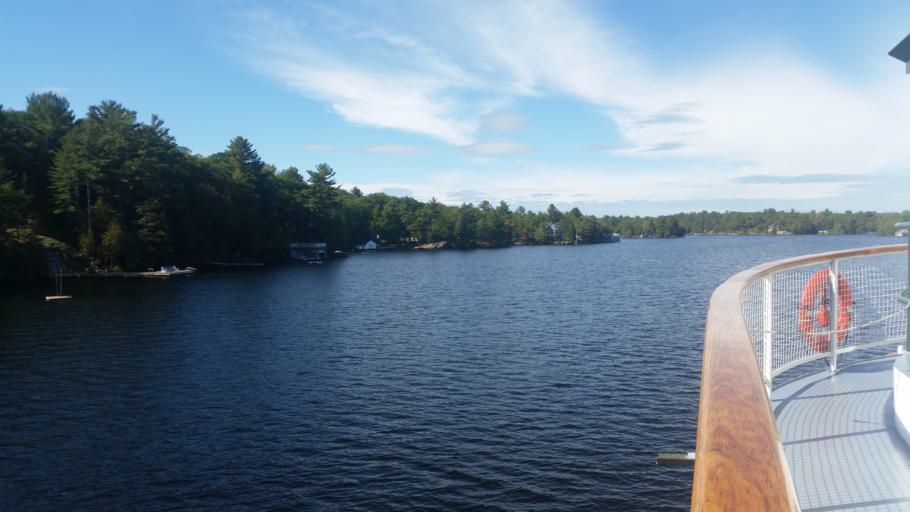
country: CA
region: Ontario
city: Gravenhurst
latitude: 44.9438
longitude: -79.4035
